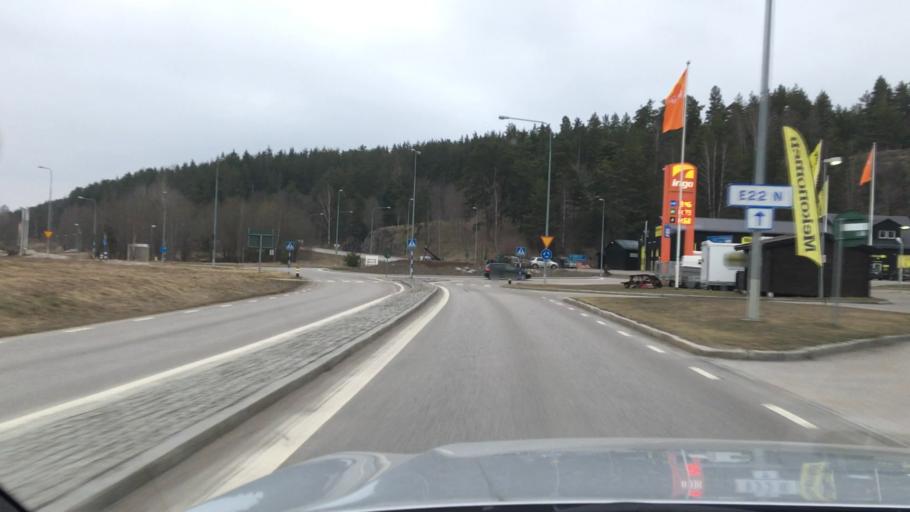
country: SE
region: OEstergoetland
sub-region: Valdemarsviks Kommun
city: Valdemarsvik
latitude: 58.2110
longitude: 16.5842
